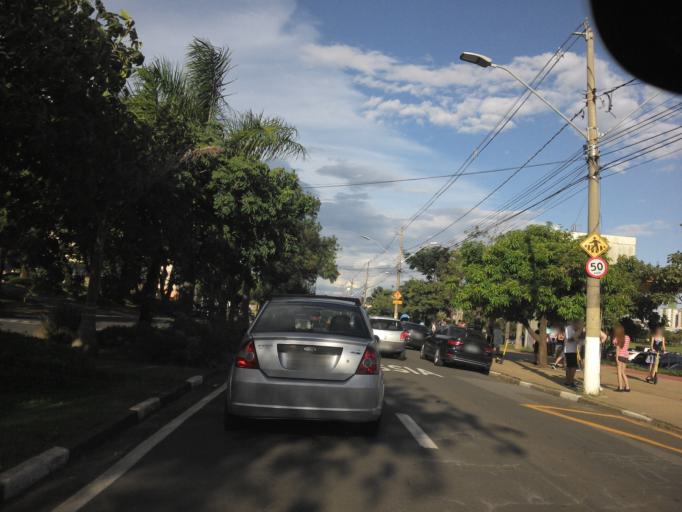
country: BR
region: Sao Paulo
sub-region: Campinas
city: Campinas
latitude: -22.8733
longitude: -47.0443
